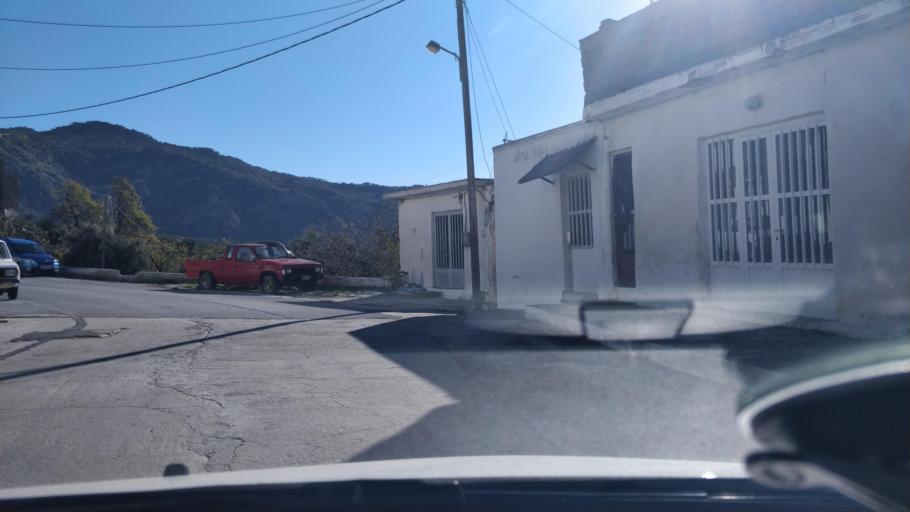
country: GR
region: Crete
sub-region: Nomos Lasithiou
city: Kritsa
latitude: 35.0791
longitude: 25.5850
